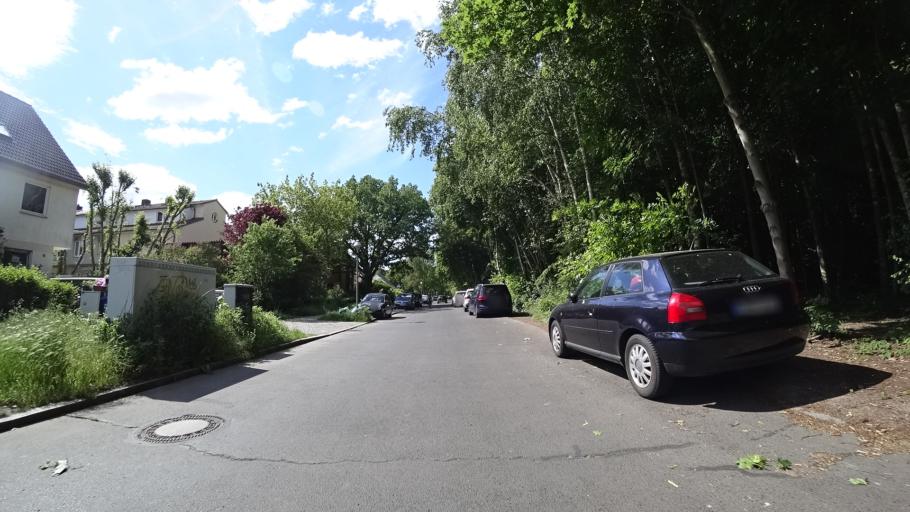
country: DE
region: Berlin
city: Lichtenrade
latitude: 52.3955
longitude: 13.3817
